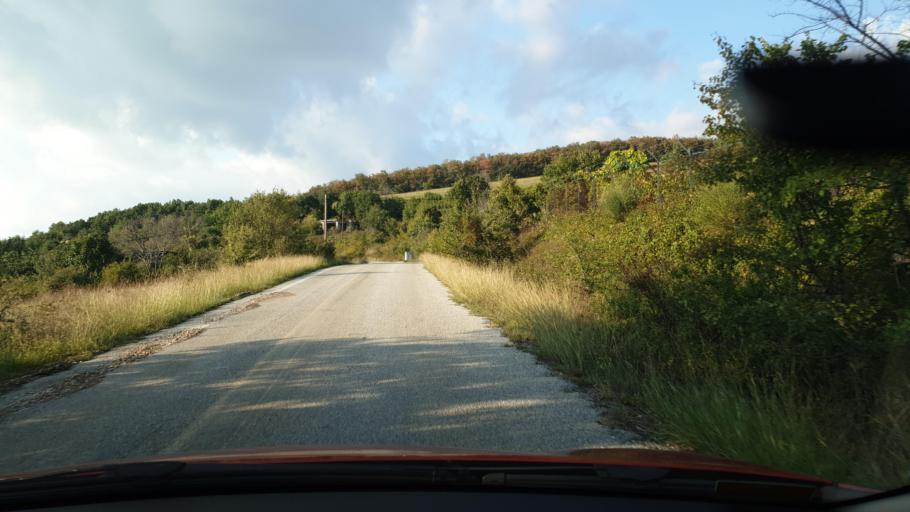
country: GR
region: Central Macedonia
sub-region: Nomos Chalkidikis
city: Galatista
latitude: 40.5271
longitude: 23.2774
